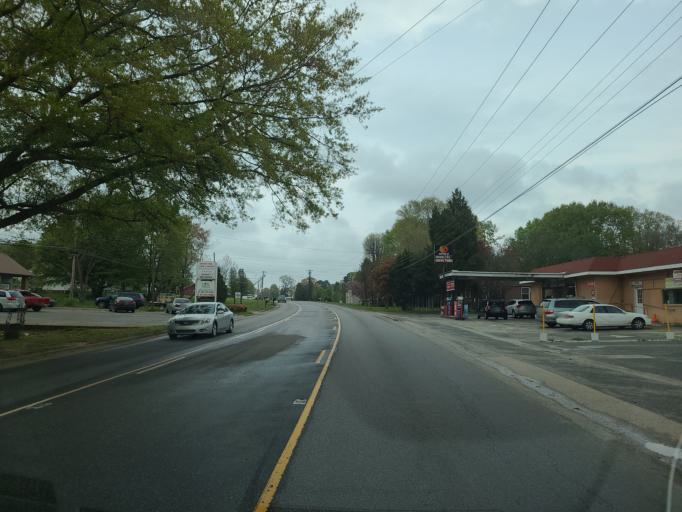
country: US
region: North Carolina
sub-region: Lincoln County
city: Lincolnton
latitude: 35.4989
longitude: -81.2420
